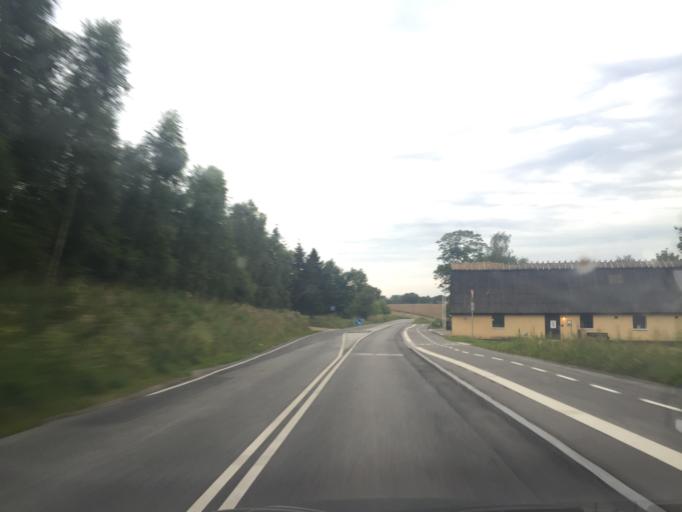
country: DK
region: Zealand
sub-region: Roskilde Kommune
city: Gundsomagle
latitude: 55.7501
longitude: 12.1388
